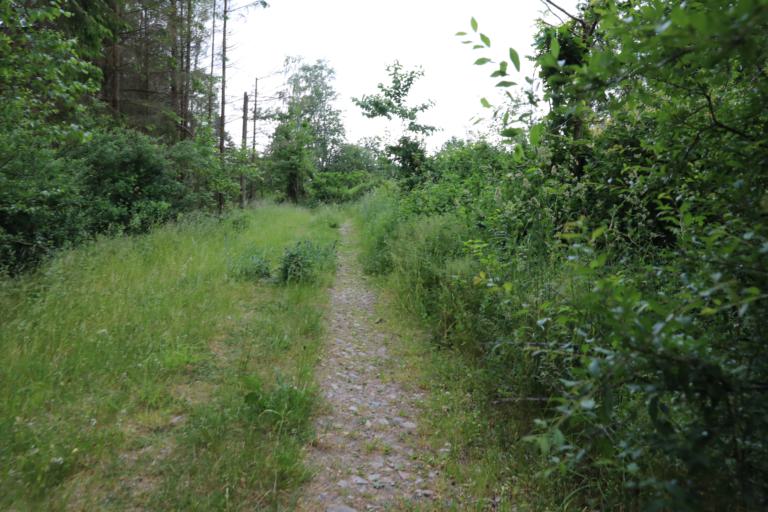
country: SE
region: Halland
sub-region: Varbergs Kommun
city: Varberg
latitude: 57.1669
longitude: 12.2623
